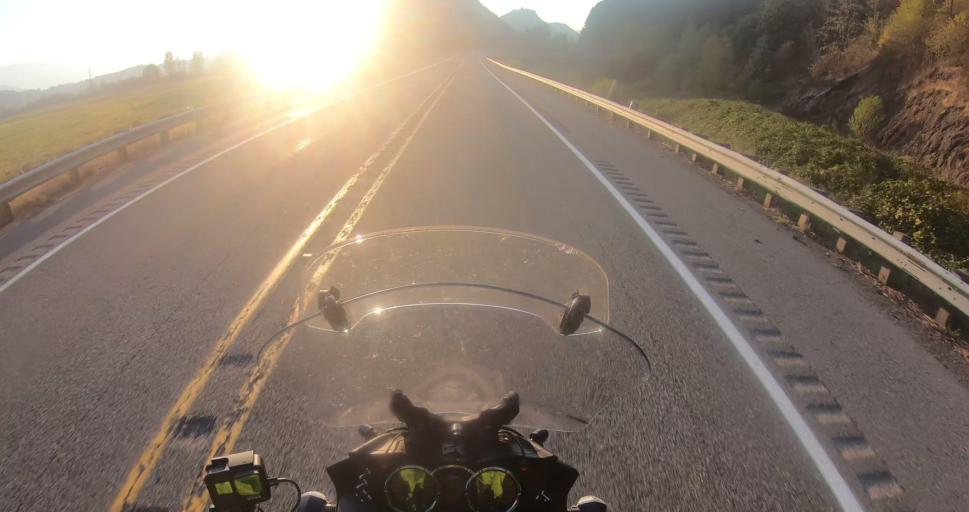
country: US
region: Washington
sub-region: Lewis County
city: Morton
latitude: 46.5370
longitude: -121.9731
